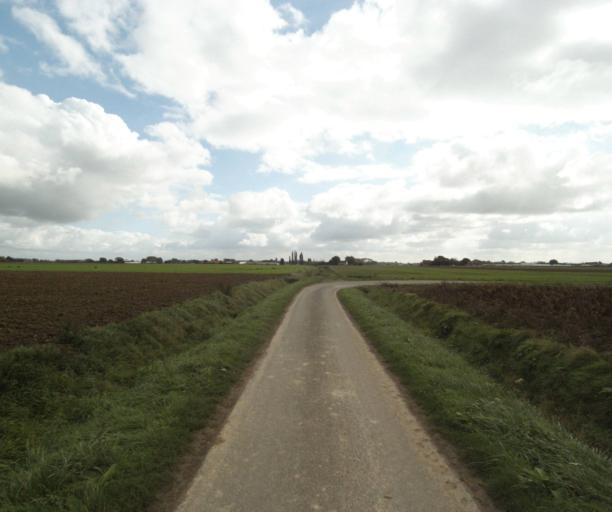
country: FR
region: Nord-Pas-de-Calais
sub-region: Departement du Nord
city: Frelinghien
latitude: 50.6953
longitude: 2.9461
